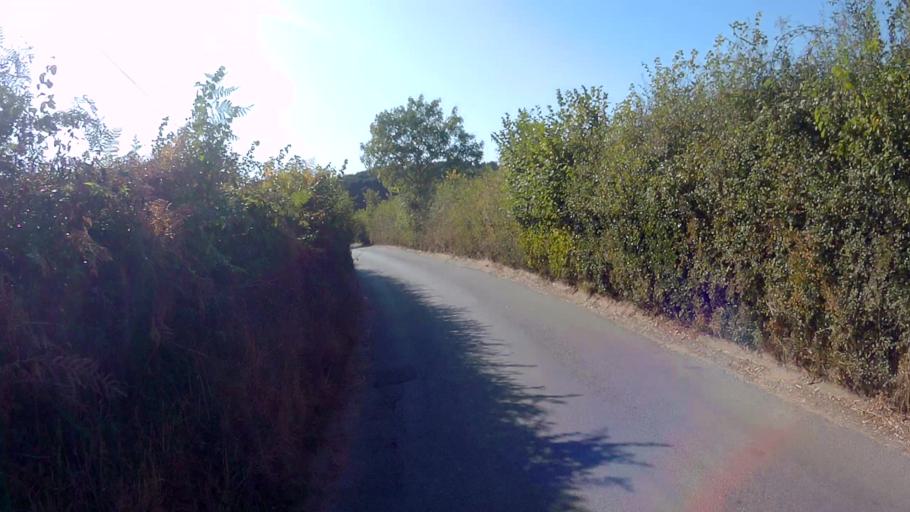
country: GB
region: England
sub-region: Surrey
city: Farnham
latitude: 51.1853
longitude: -0.7582
